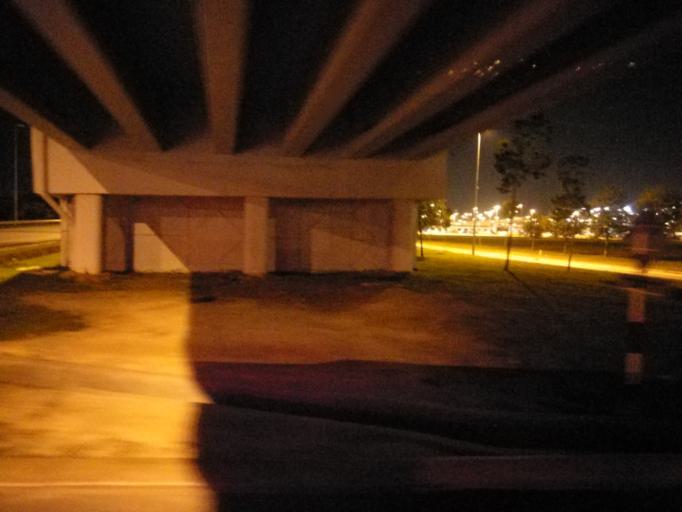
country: MY
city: Sungai Pelek New Village
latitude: 2.7484
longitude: 101.6820
